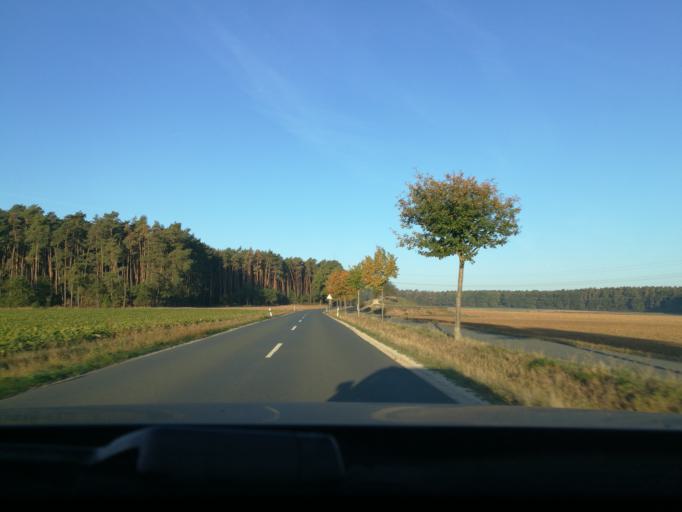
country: DE
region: Bavaria
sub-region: Regierungsbezirk Mittelfranken
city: Obermichelbach
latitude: 49.5288
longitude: 10.8935
